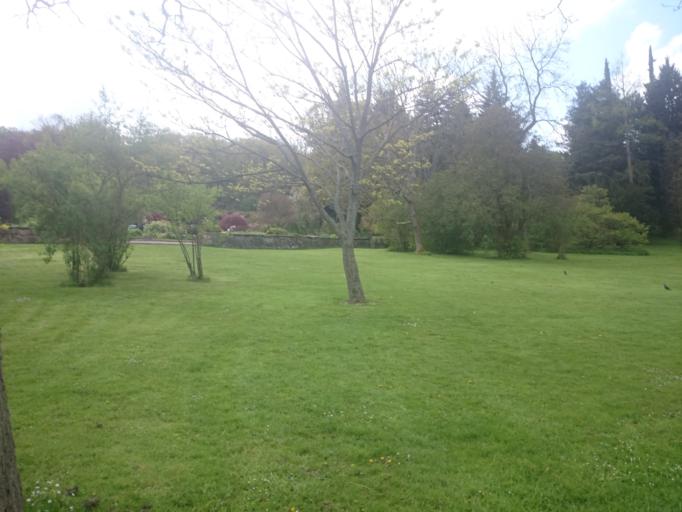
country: SE
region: Vaestra Goetaland
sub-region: Goteborg
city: Goeteborg
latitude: 57.6812
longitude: 11.9546
